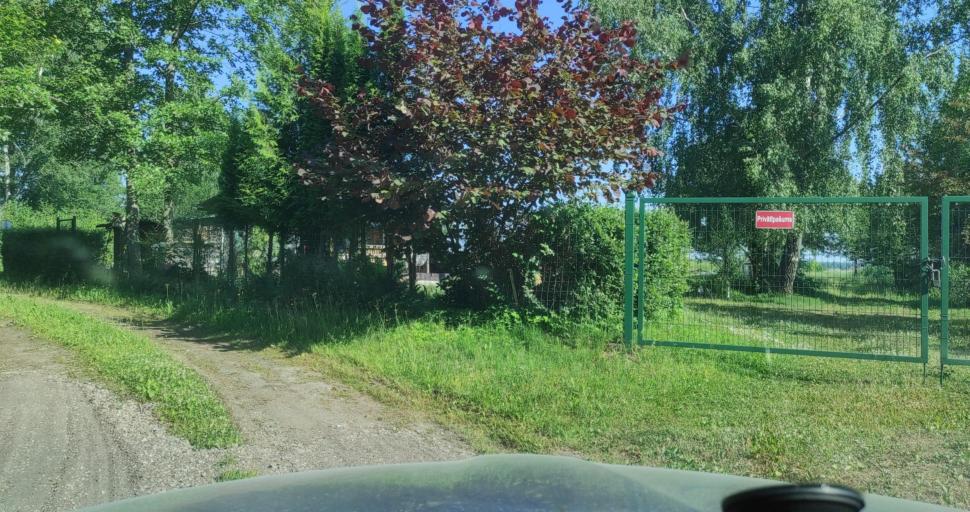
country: LV
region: Jurmala
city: Jurmala
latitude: 56.9576
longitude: 23.7972
